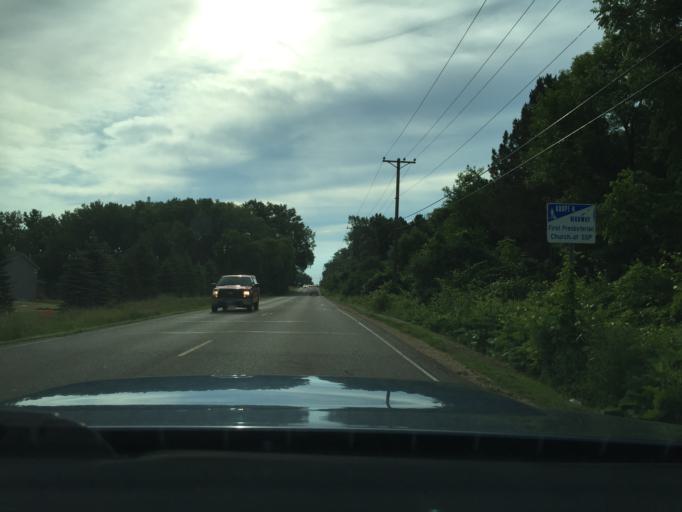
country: US
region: Minnesota
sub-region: Dakota County
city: West Saint Paul
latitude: 44.8980
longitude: -93.1007
